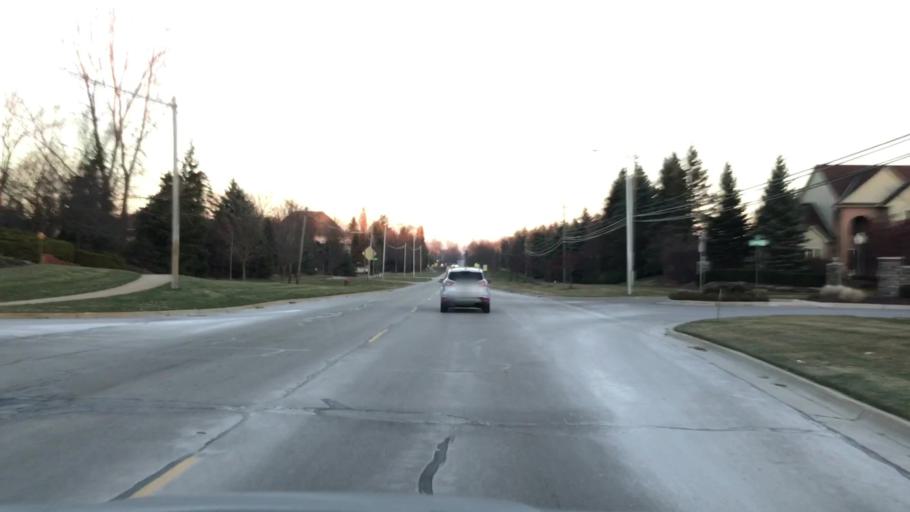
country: US
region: Michigan
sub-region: Wayne County
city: Northville
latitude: 42.4510
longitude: -83.5106
